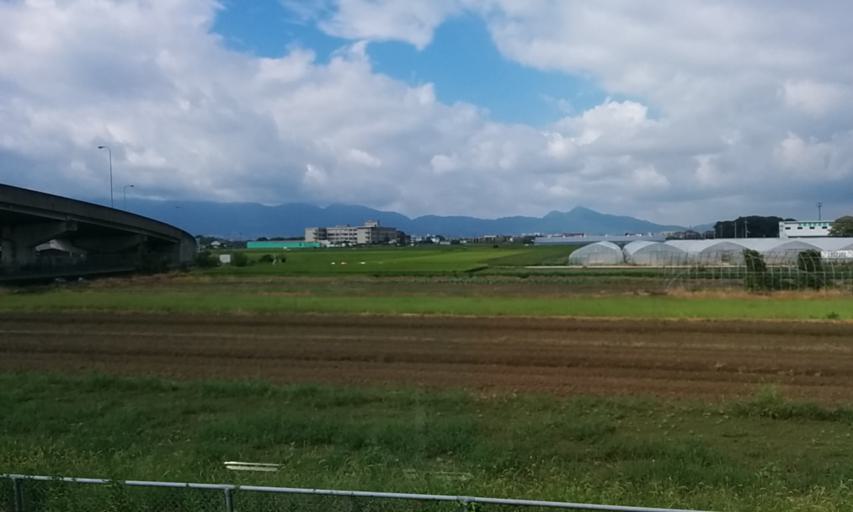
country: JP
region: Nara
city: Tawaramoto
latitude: 34.5322
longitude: 135.7942
